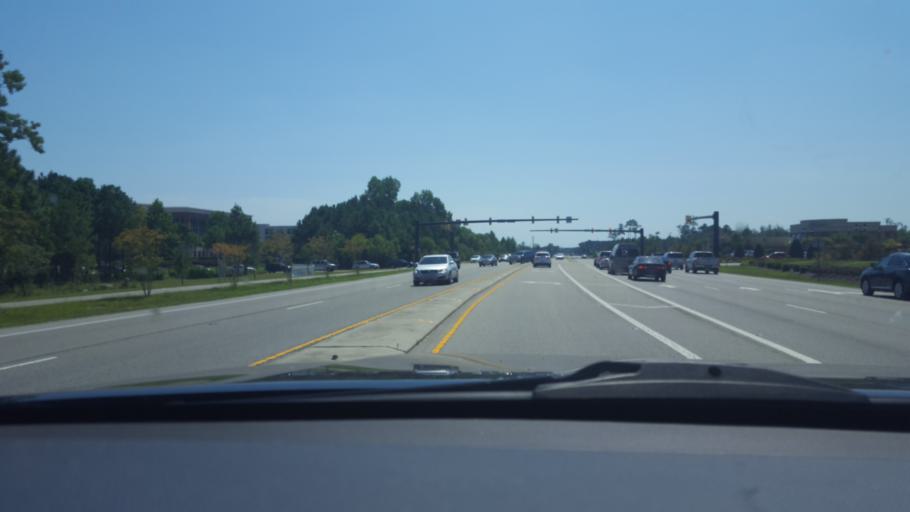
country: US
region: North Carolina
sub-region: New Hanover County
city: Ogden
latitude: 34.2433
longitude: -77.8277
